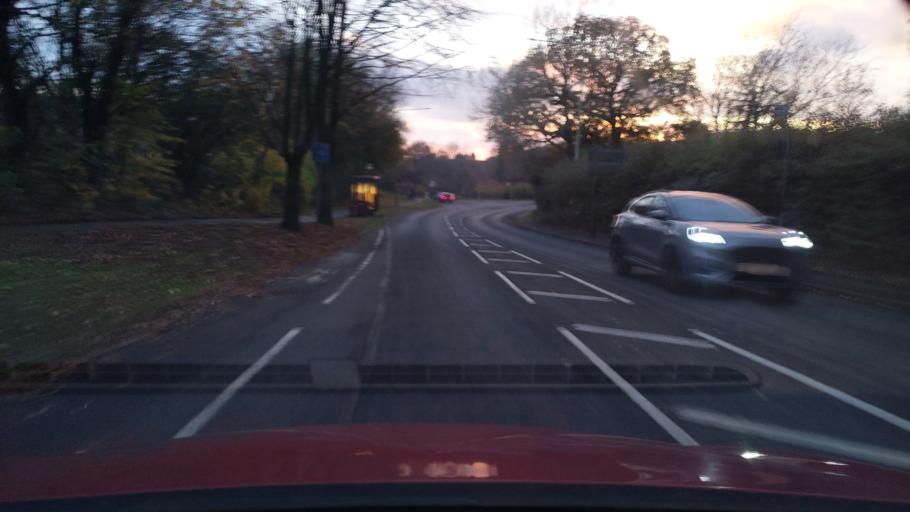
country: GB
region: England
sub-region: Lancashire
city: Clayton-le-Woods
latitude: 53.7052
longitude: -2.6446
